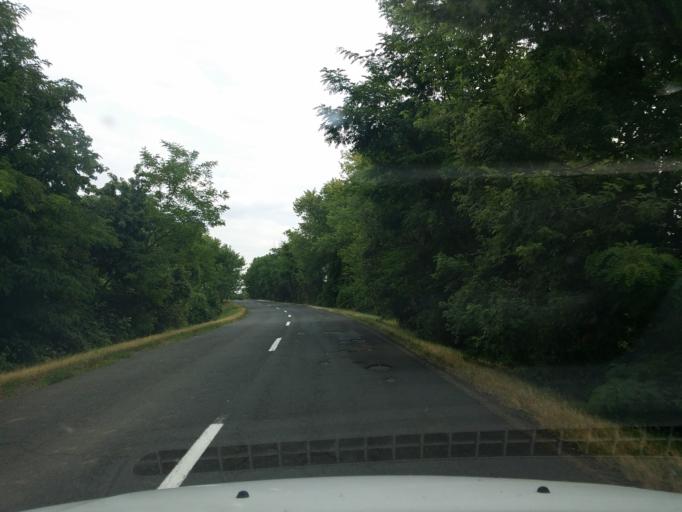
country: HU
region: Nograd
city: Bercel
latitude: 47.9267
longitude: 19.3622
